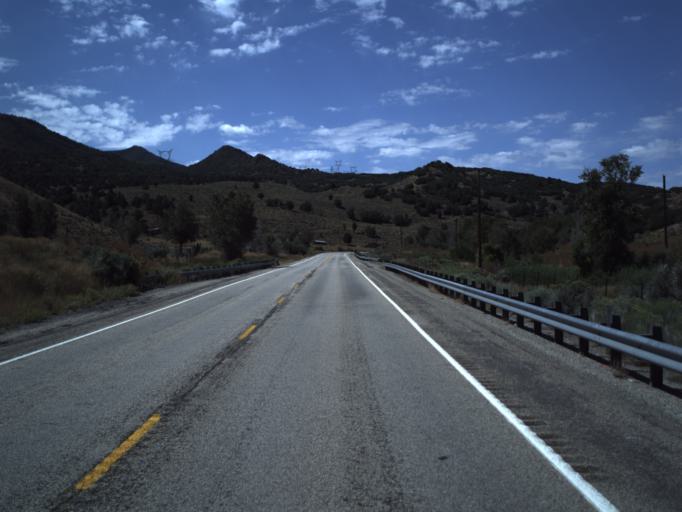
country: US
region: Utah
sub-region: Utah County
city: Woodland Hills
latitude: 39.9701
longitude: -111.5088
